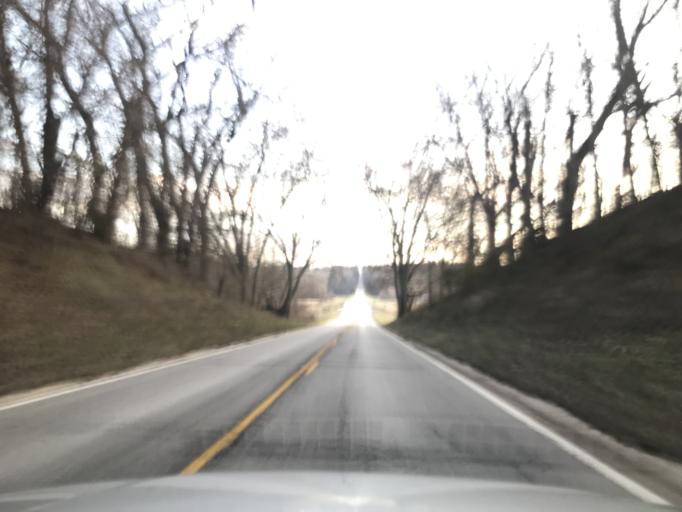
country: US
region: Illinois
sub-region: Henderson County
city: Oquawka
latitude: 41.0085
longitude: -90.8535
